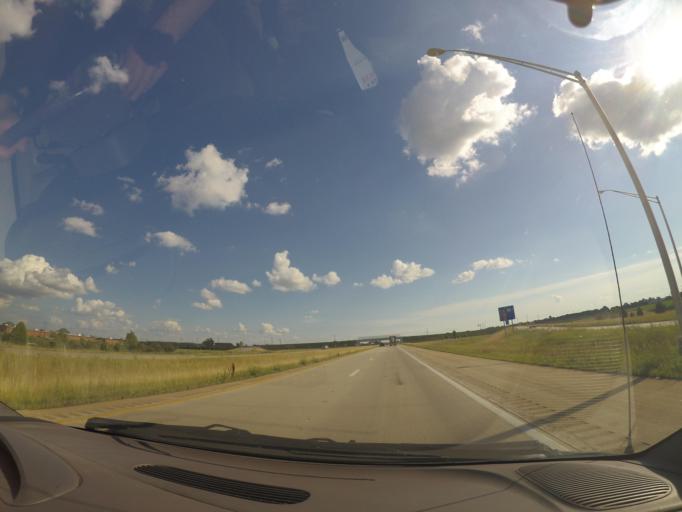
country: US
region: Ohio
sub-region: Lucas County
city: Waterville
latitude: 41.5117
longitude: -83.7525
